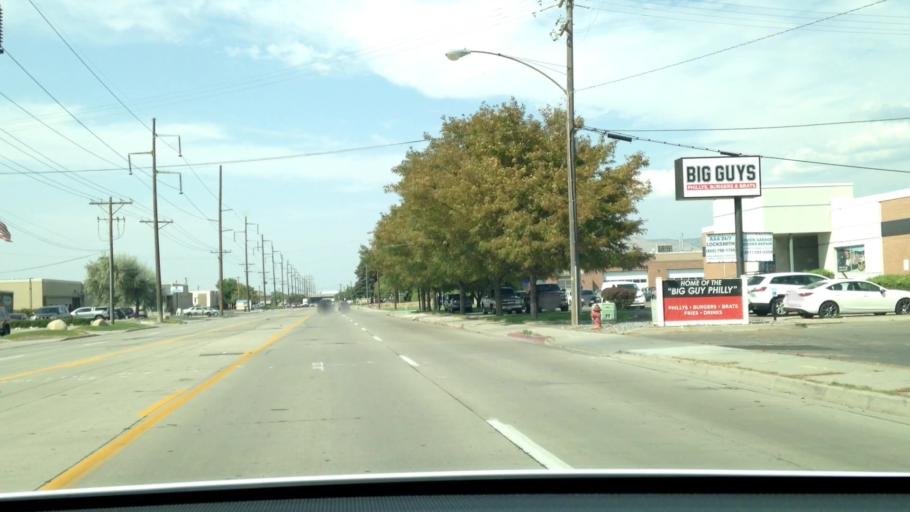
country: US
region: Utah
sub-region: Salt Lake County
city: South Salt Lake
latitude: 40.7154
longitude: -111.9174
